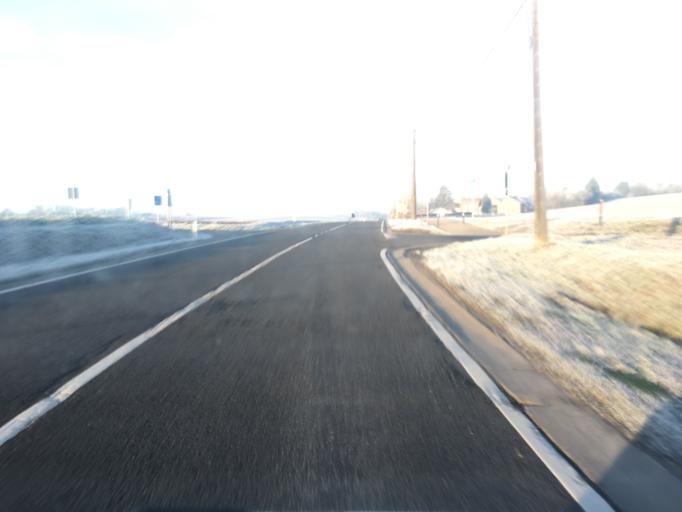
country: BE
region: Wallonia
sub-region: Province de Liege
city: Wanze
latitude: 50.5404
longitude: 5.1607
